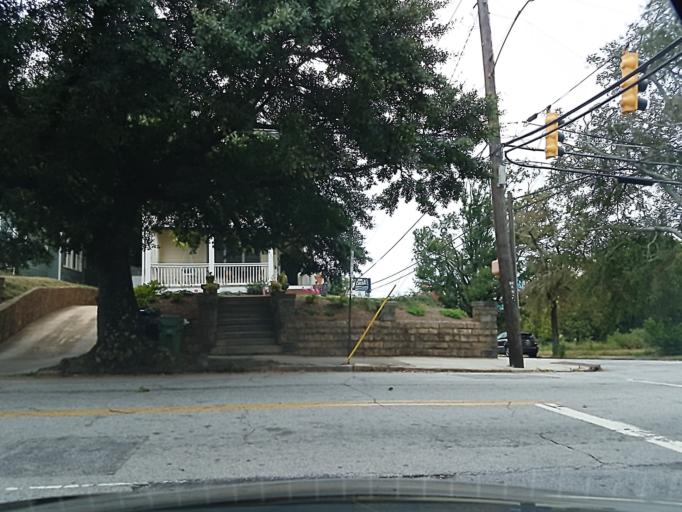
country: US
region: Georgia
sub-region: Fulton County
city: Atlanta
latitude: 33.7578
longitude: -84.3764
